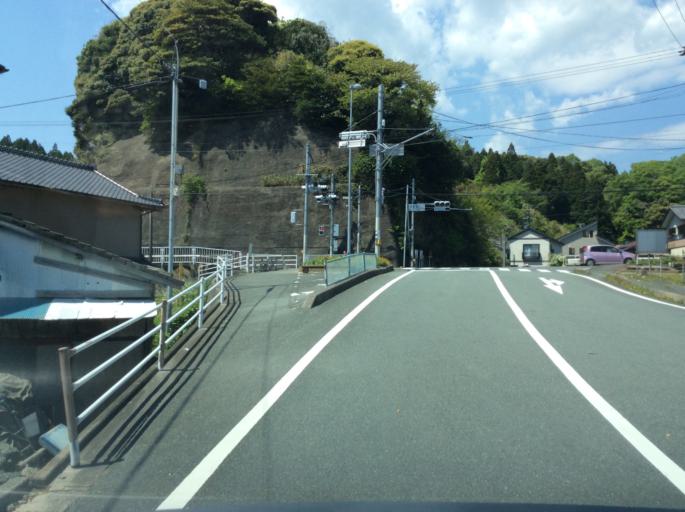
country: JP
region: Ibaraki
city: Kitaibaraki
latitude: 36.8591
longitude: 140.7893
